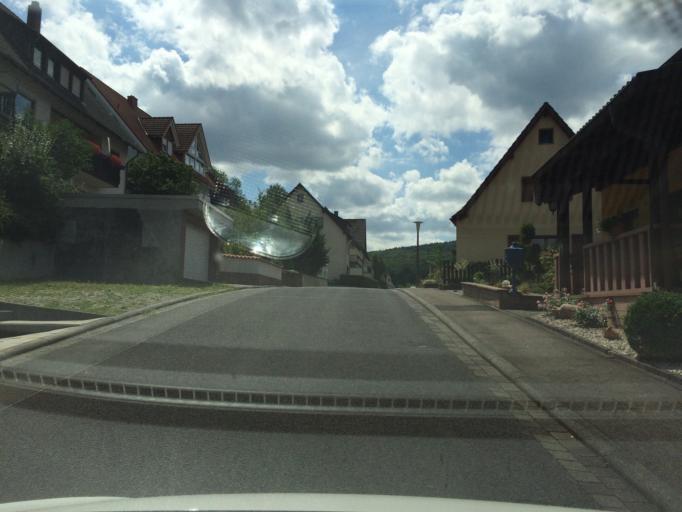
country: DE
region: Bavaria
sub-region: Regierungsbezirk Unterfranken
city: Haibach
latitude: 49.9490
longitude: 9.2530
